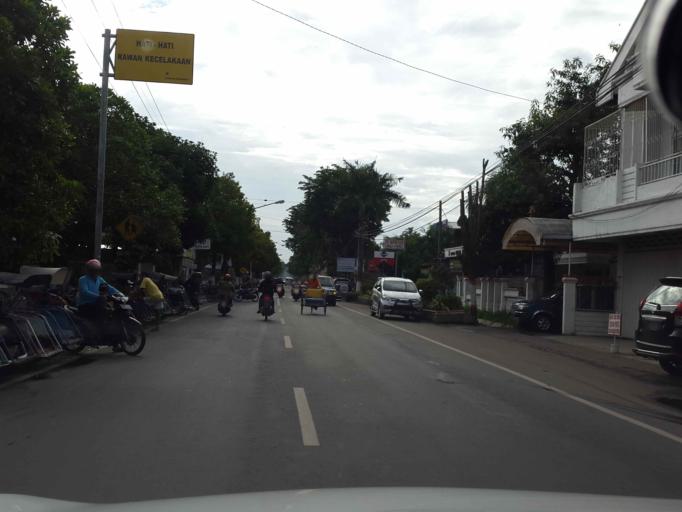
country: ID
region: East Java
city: Soko
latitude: -7.4807
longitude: 112.4322
